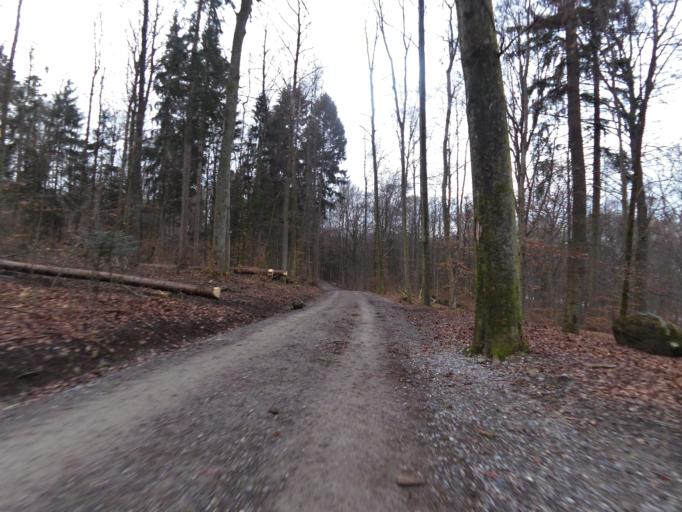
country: CH
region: Zurich
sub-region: Bezirk Dietikon
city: Schlieren / Boden
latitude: 47.3892
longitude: 8.4591
